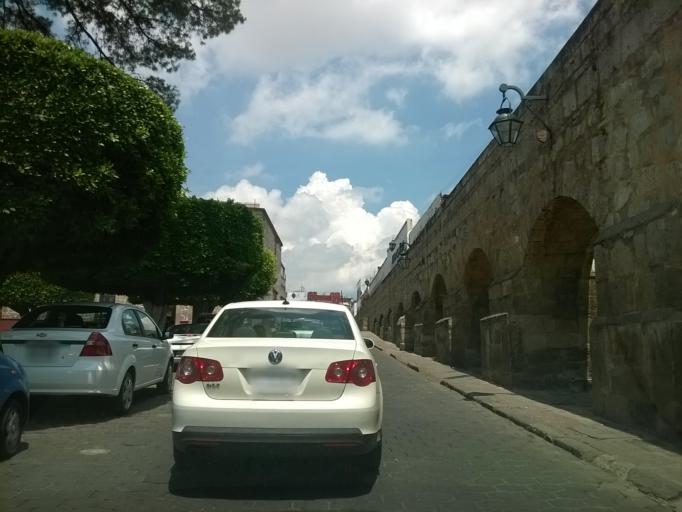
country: MX
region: Michoacan
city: Morelia
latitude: 19.7035
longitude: -101.1827
